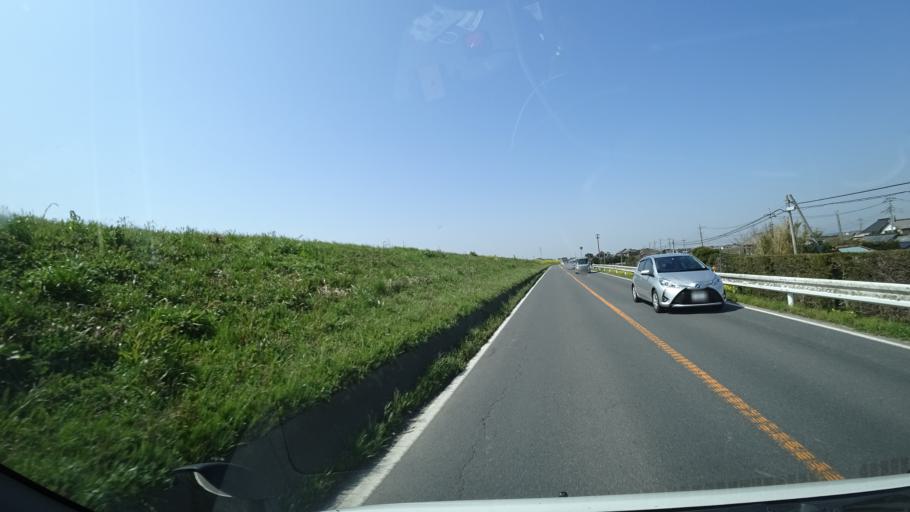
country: JP
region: Chiba
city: Katori-shi
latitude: 35.9130
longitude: 140.4319
